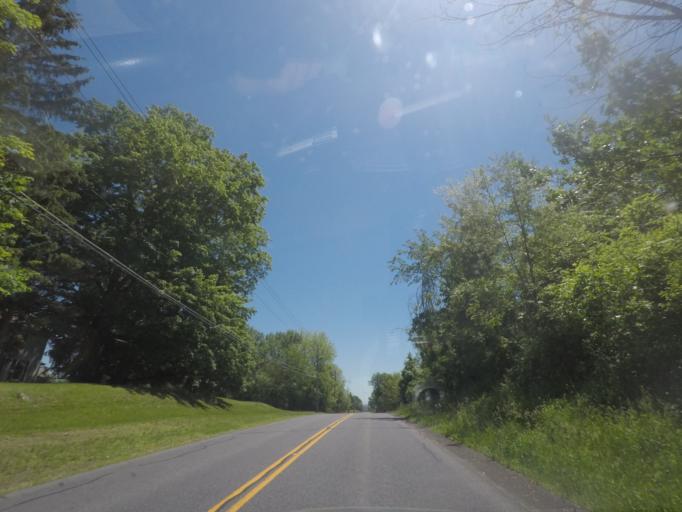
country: US
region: New York
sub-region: Saratoga County
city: Mechanicville
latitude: 42.9383
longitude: -73.6940
